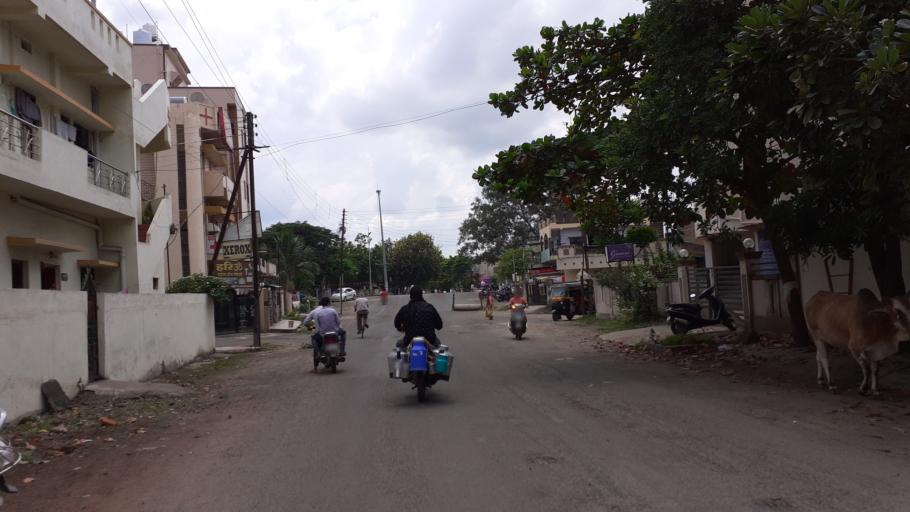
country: IN
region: Maharashtra
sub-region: Nagpur Division
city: Nagpur
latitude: 21.1081
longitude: 79.1170
